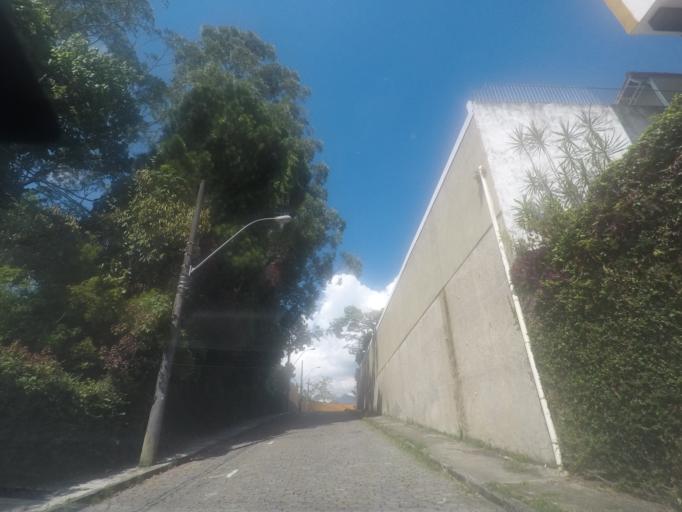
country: BR
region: Rio de Janeiro
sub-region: Petropolis
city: Petropolis
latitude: -22.5086
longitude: -43.1793
